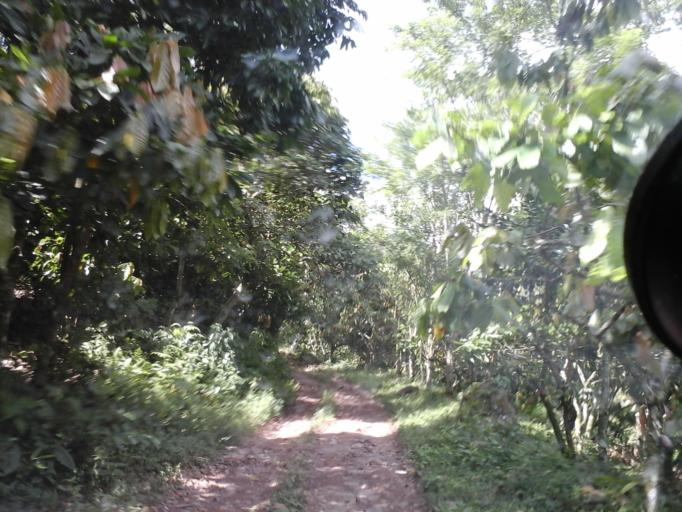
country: CO
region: Cesar
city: San Diego
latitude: 10.2856
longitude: -73.0865
